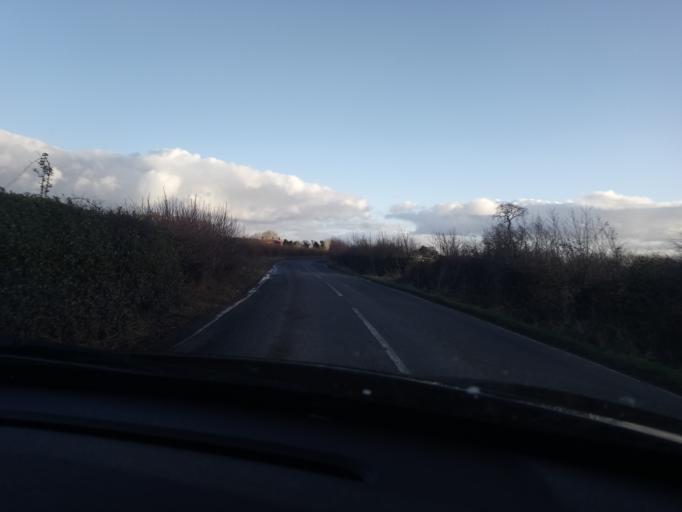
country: GB
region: England
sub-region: Shropshire
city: Petton
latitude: 52.8986
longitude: -2.8038
